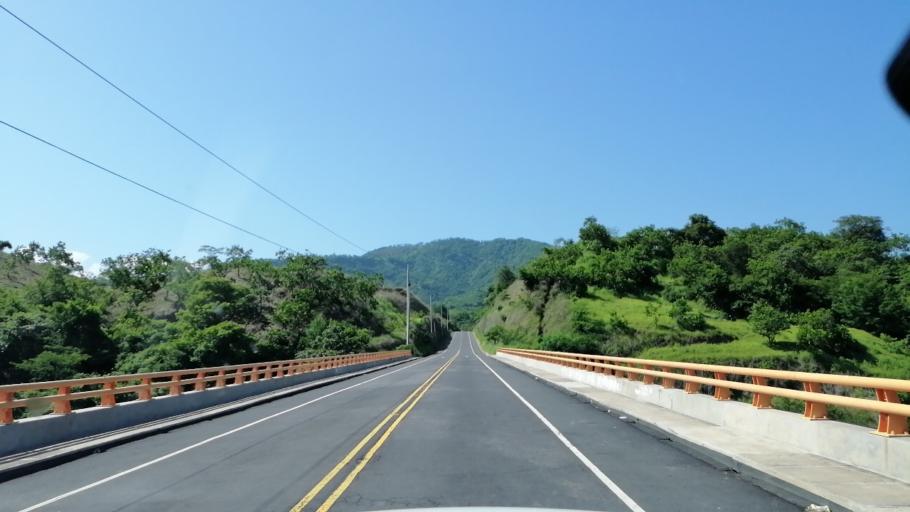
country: HN
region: Lempira
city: La Virtud
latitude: 13.9972
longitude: -88.7479
